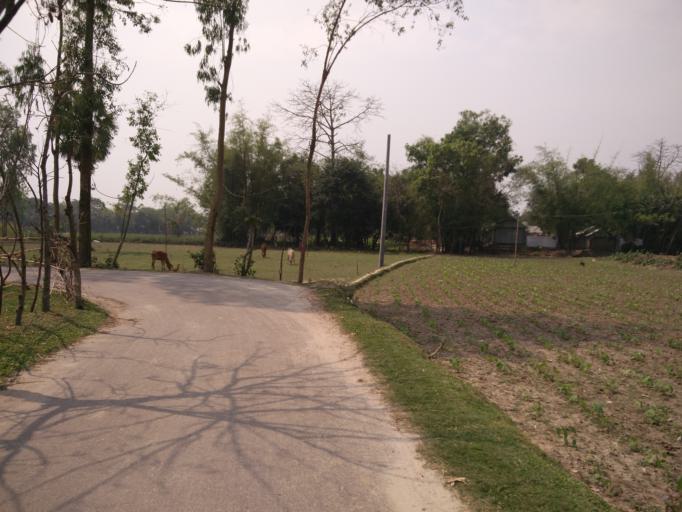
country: BD
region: Dhaka
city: Muktagacha
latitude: 24.8886
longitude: 90.2711
